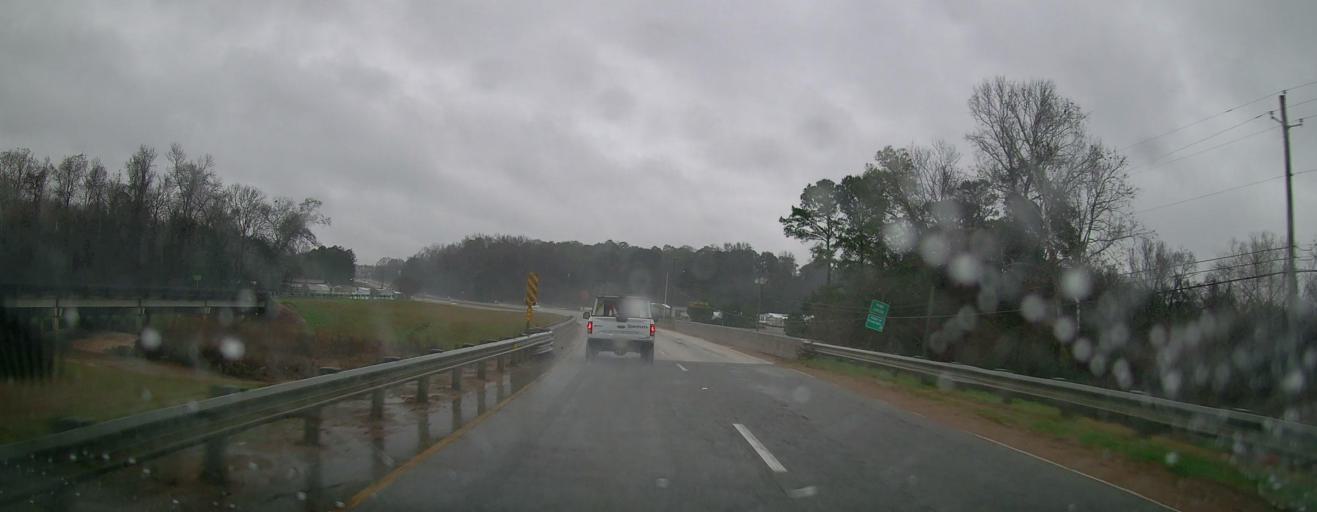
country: US
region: Alabama
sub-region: Autauga County
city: Prattville
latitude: 32.4252
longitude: -86.4116
